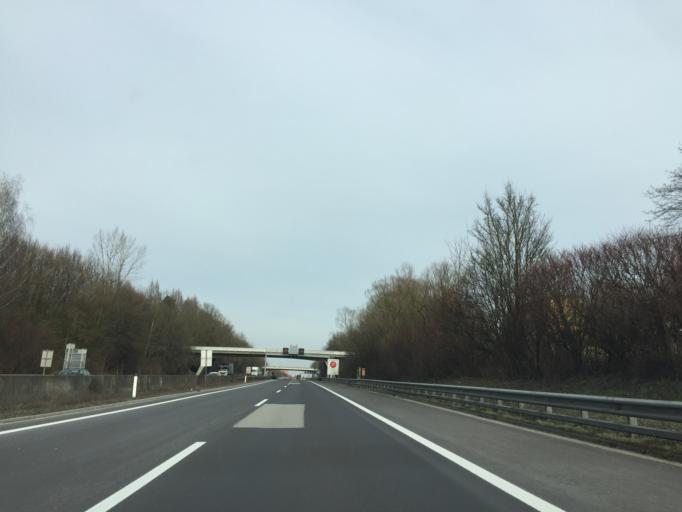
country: AT
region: Upper Austria
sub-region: Politischer Bezirk Scharding
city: Sankt Marienkirchen bei Schaerding
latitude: 48.3919
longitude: 13.4242
